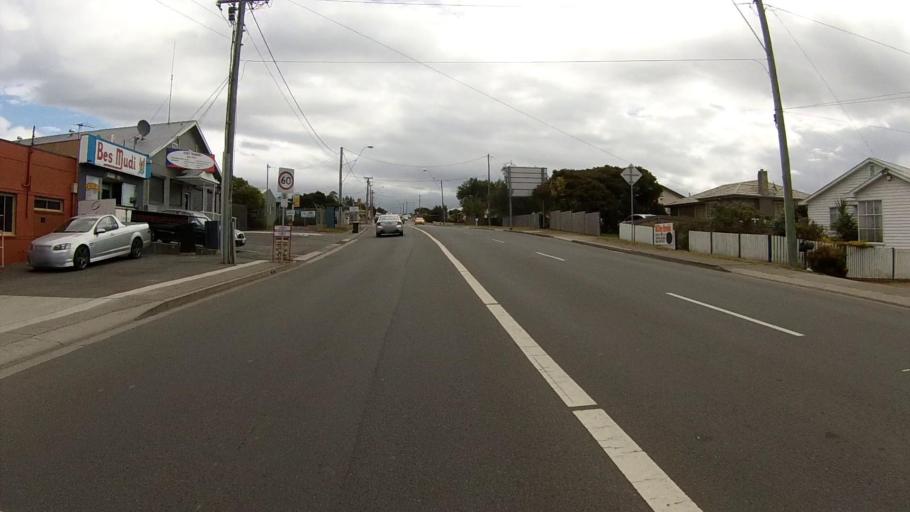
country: AU
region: Tasmania
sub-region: Clarence
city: Warrane
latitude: -42.8568
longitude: 147.3931
